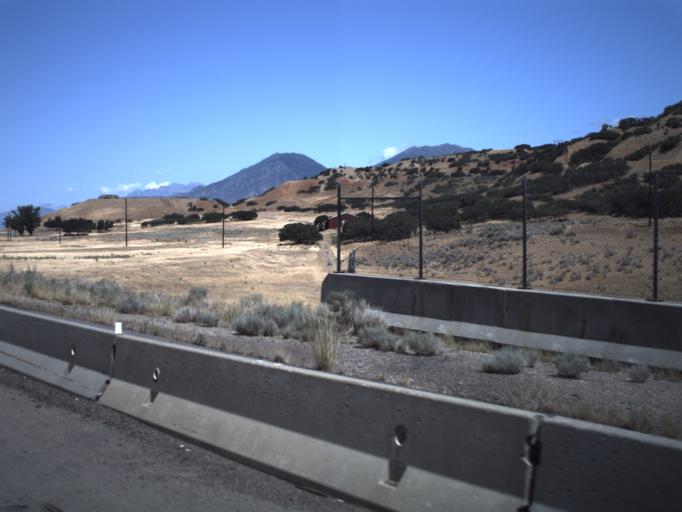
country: US
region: Utah
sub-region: Utah County
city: Mapleton
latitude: 40.0753
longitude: -111.5805
